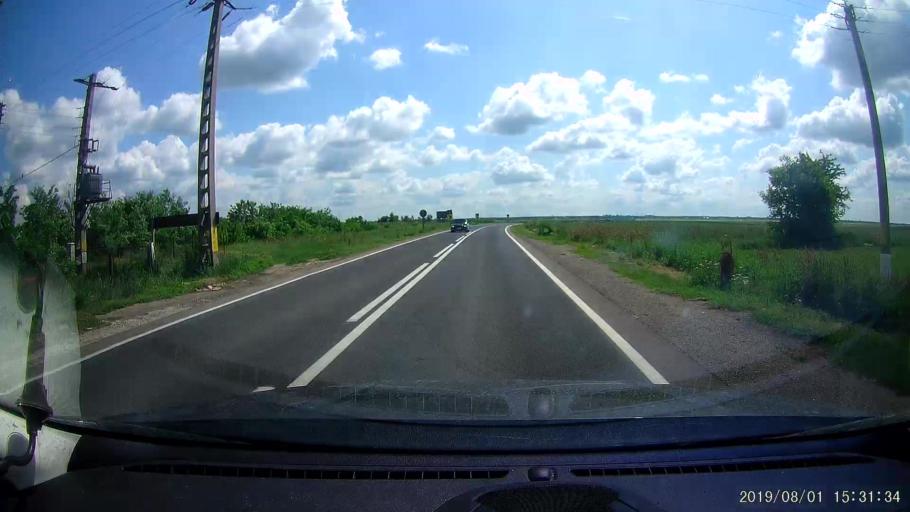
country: RO
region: Braila
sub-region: Comuna Insuratei
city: Insuratei
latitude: 44.9435
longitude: 27.6570
